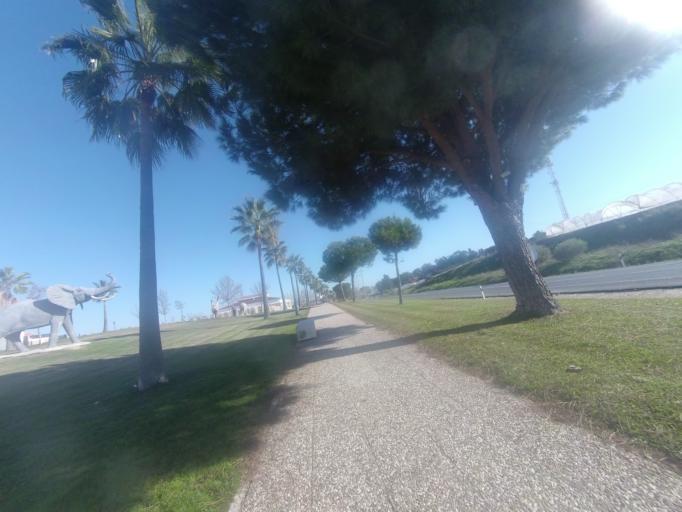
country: ES
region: Andalusia
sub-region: Provincia de Huelva
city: Palos de la Frontera
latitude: 37.2236
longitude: -6.8991
